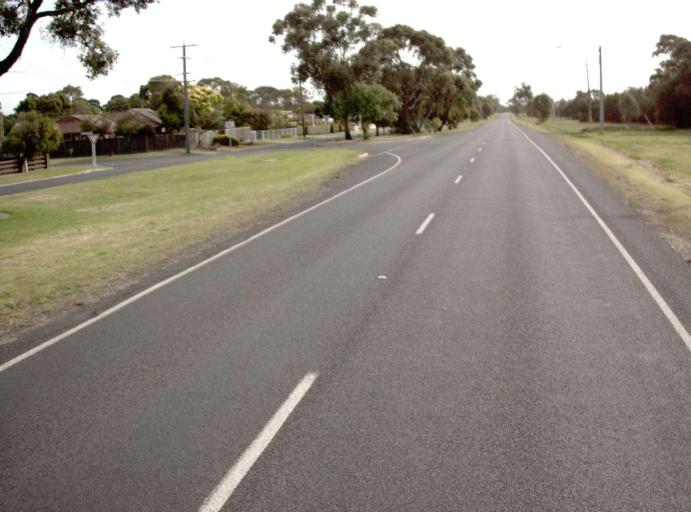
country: AU
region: Victoria
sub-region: Latrobe
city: Traralgon
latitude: -38.1216
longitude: 146.5726
